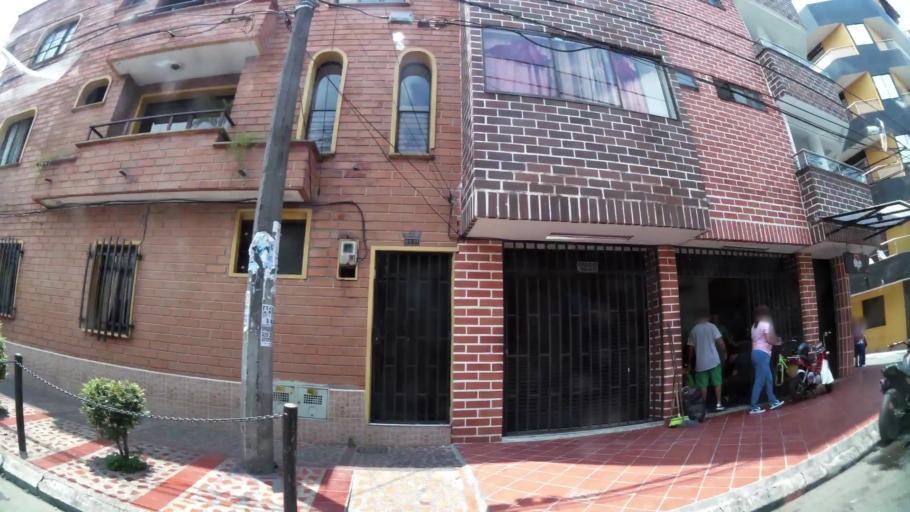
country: CO
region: Antioquia
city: Itagui
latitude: 6.1720
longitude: -75.6139
